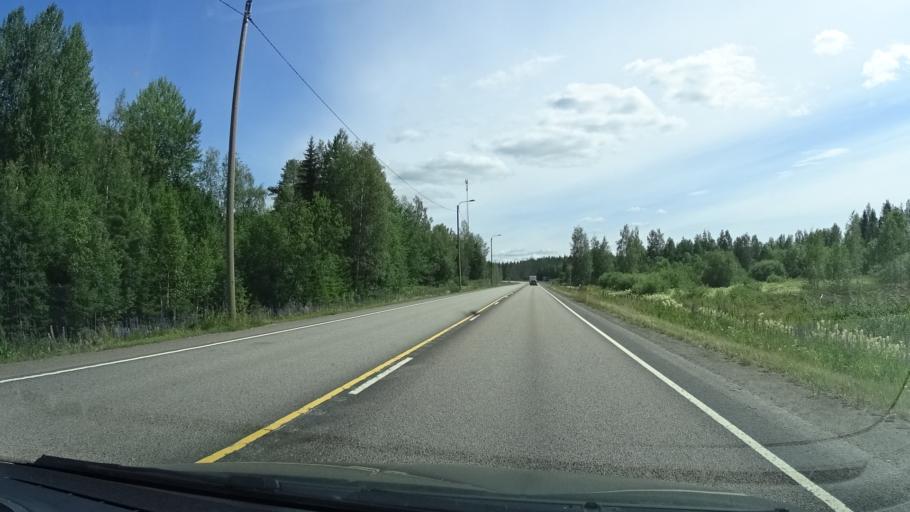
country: FI
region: Central Finland
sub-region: Jyvaeskylae
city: Uurainen
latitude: 62.2651
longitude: 25.4631
